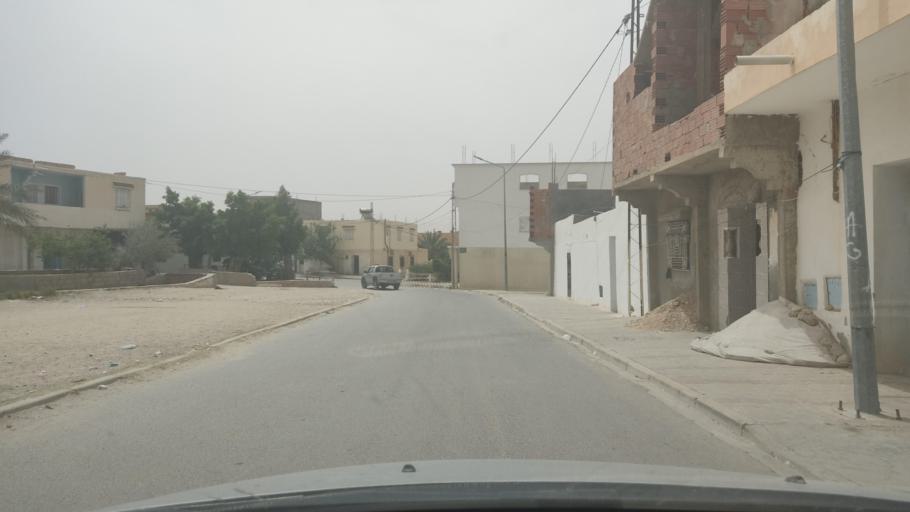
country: TN
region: Gafsa
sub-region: Gafsa Municipality
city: Gafsa
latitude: 34.3340
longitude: 8.9543
